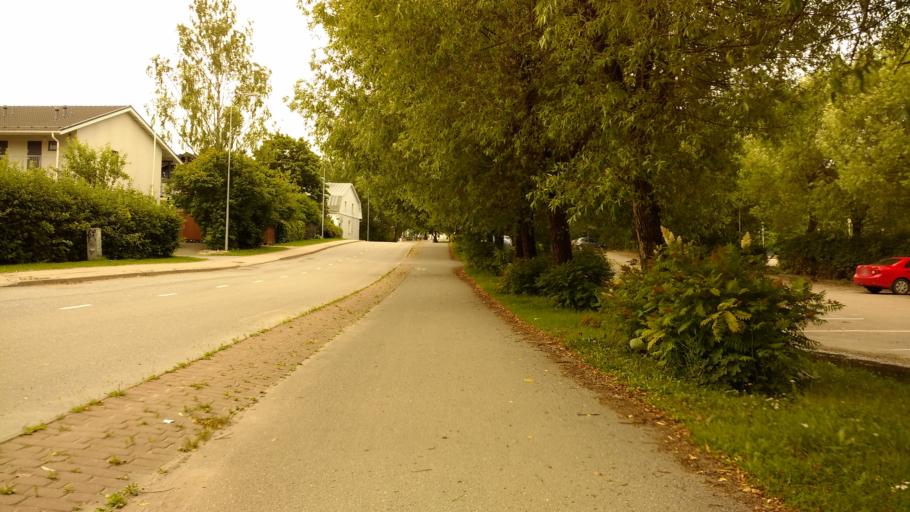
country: FI
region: Varsinais-Suomi
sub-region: Turku
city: Turku
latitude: 60.4570
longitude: 22.2886
